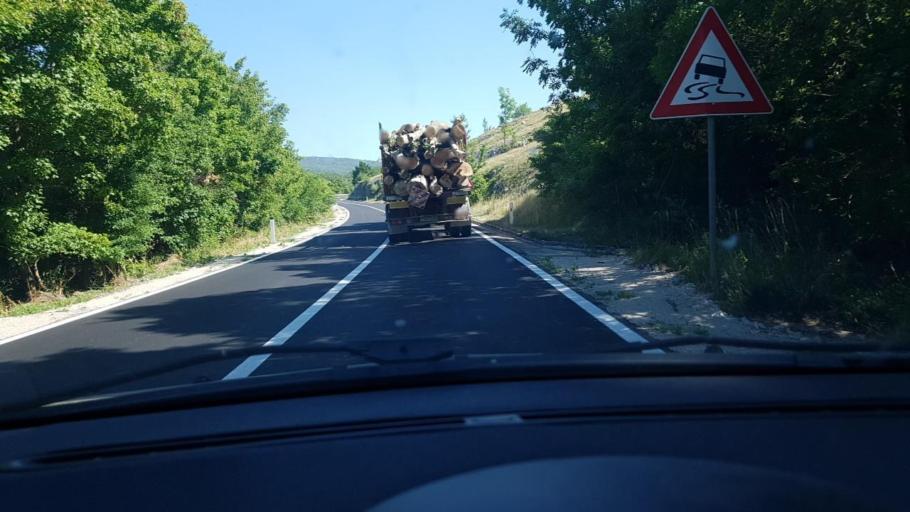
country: BA
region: Federation of Bosnia and Herzegovina
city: Bosansko Grahovo
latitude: 44.2972
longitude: 16.3046
